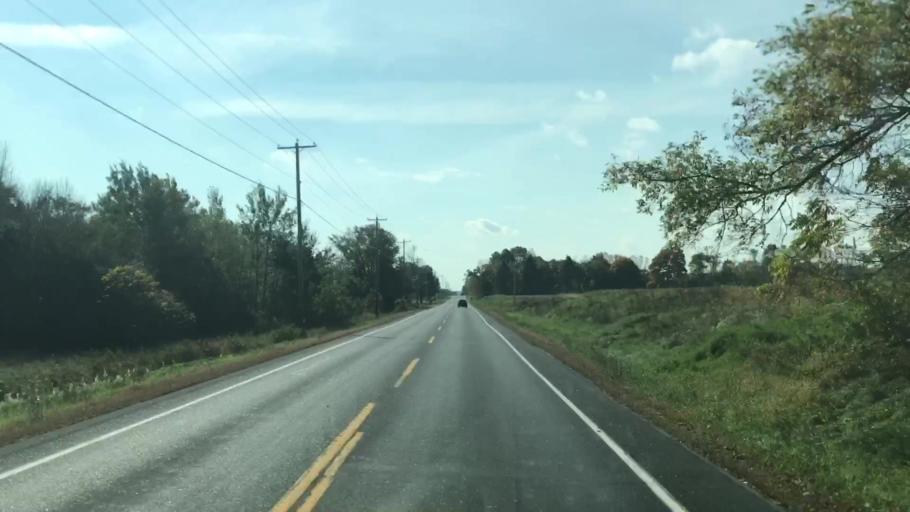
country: US
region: Wisconsin
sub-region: Ozaukee County
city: Mequon
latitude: 43.2171
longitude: -88.0435
